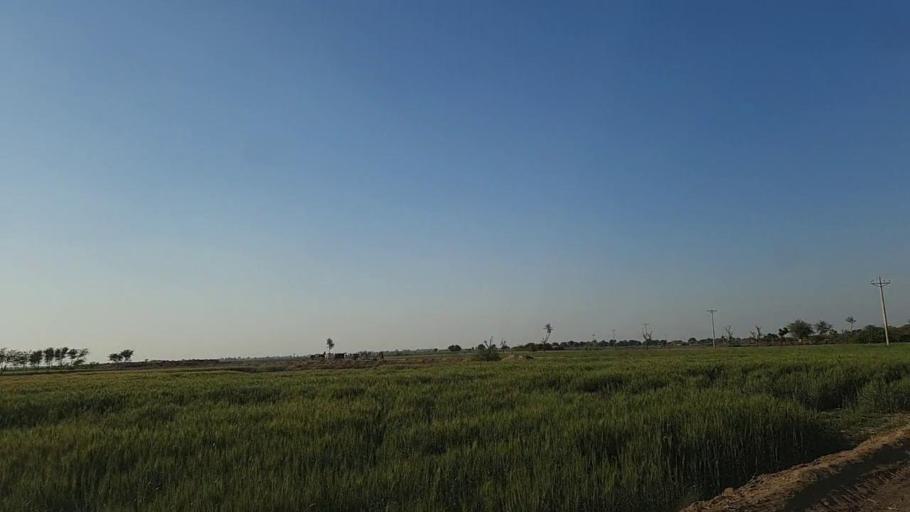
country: PK
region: Sindh
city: Samaro
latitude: 25.3494
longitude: 69.3634
